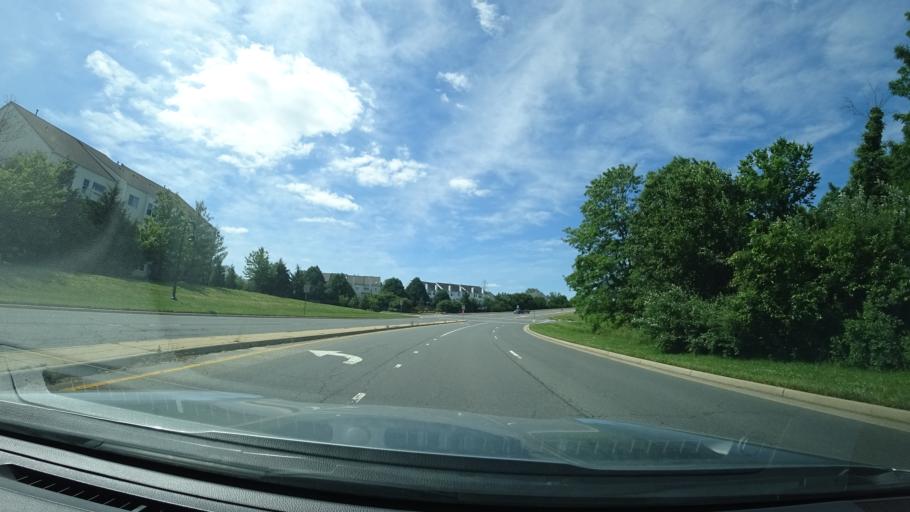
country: US
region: Virginia
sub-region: Loudoun County
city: Sterling
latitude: 39.0113
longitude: -77.4290
